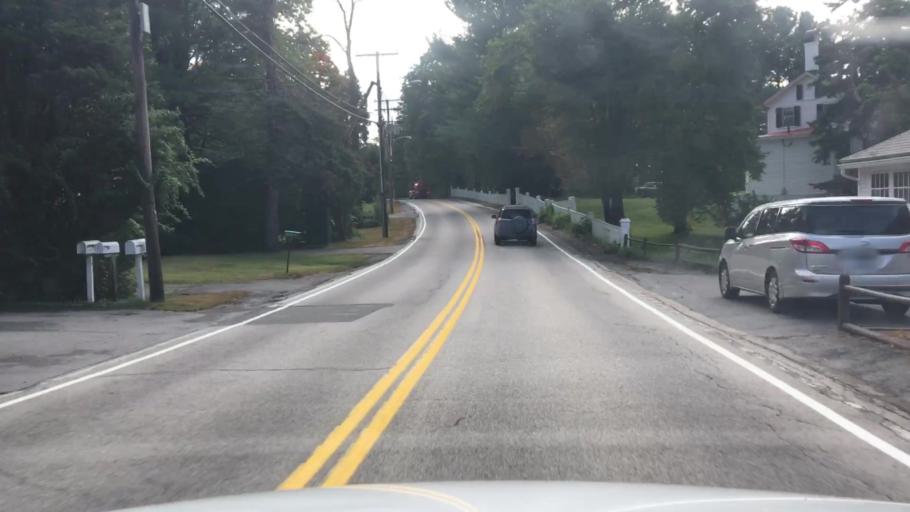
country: US
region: Maine
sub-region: York County
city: Kittery
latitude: 43.0859
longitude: -70.7311
